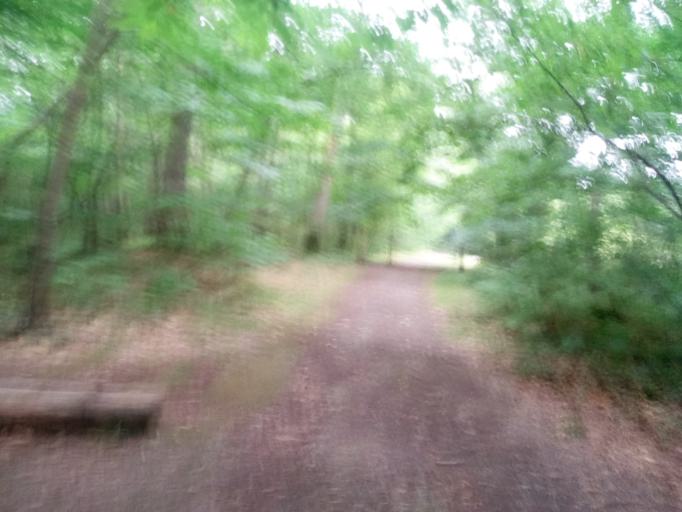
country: FR
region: Lower Normandy
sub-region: Departement du Calvados
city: Clinchamps-sur-Orne
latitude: 49.0434
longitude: -0.4263
